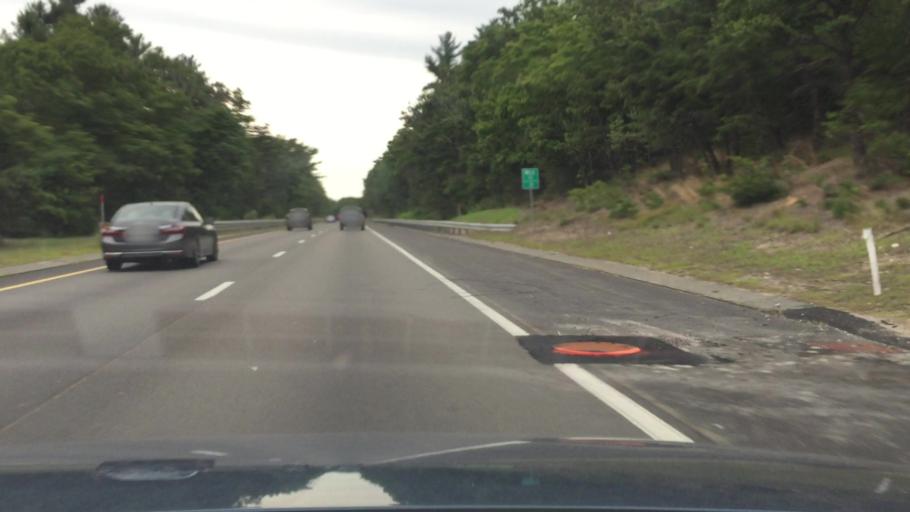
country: US
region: Massachusetts
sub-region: Plymouth County
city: Plymouth
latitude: 41.9247
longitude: -70.6291
